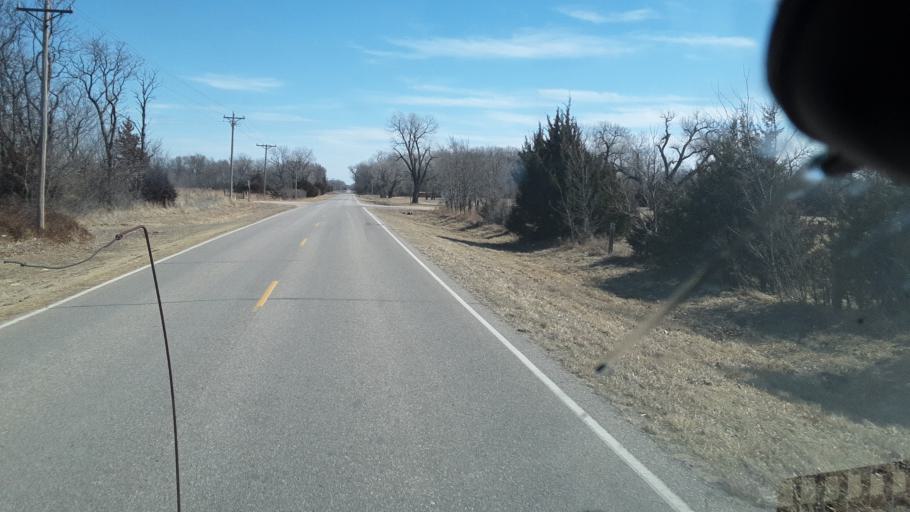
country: US
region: Kansas
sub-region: Reno County
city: Hutchinson
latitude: 38.1593
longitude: -97.9053
